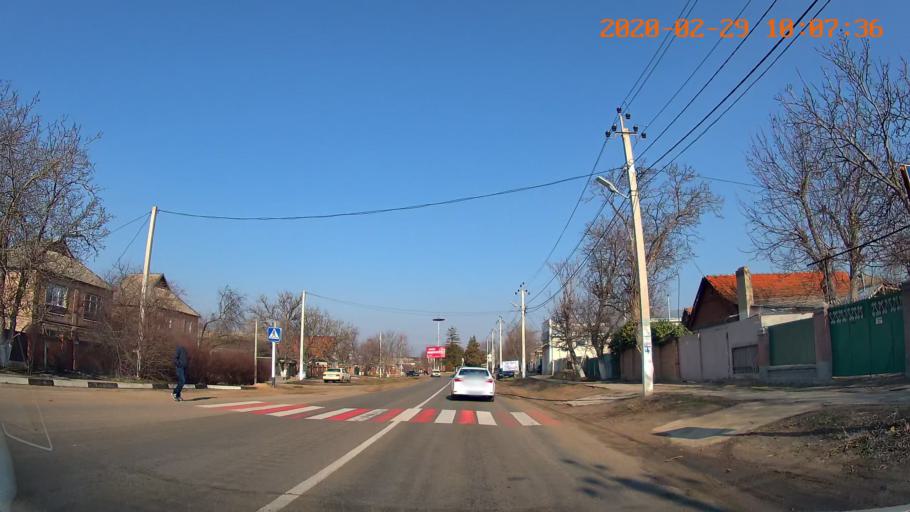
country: MD
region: Telenesti
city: Tiraspolul Nou
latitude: 46.8220
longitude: 29.6643
